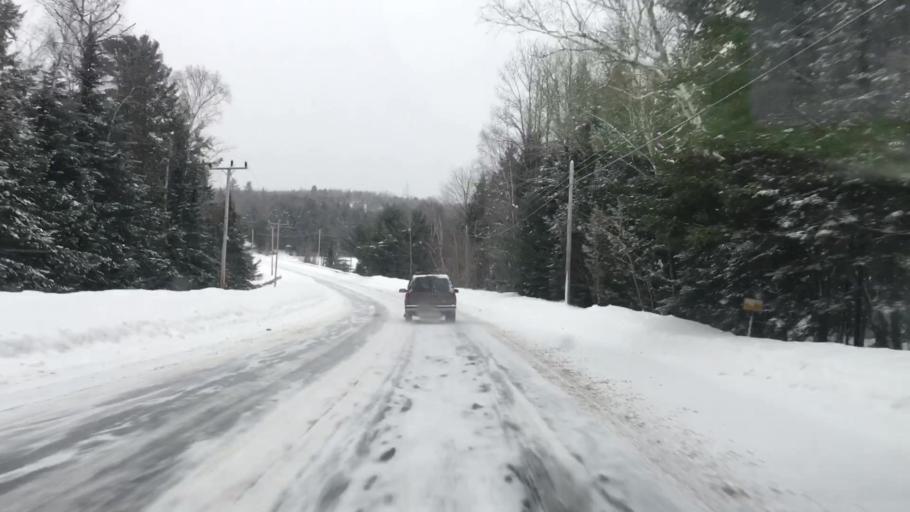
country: US
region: Maine
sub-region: Penobscot County
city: Medway
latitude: 45.6003
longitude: -68.4652
